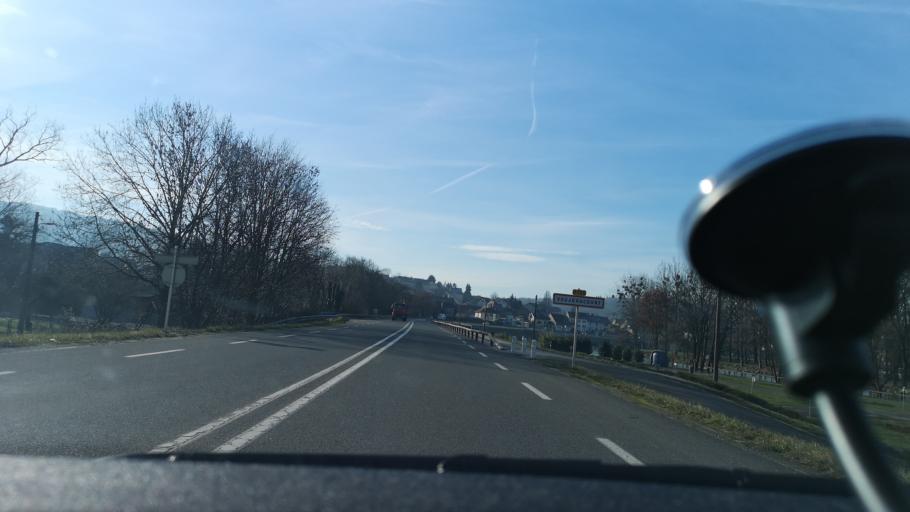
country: FR
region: Franche-Comte
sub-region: Departement du Doubs
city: Voujeaucourt
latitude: 47.4760
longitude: 6.7721
